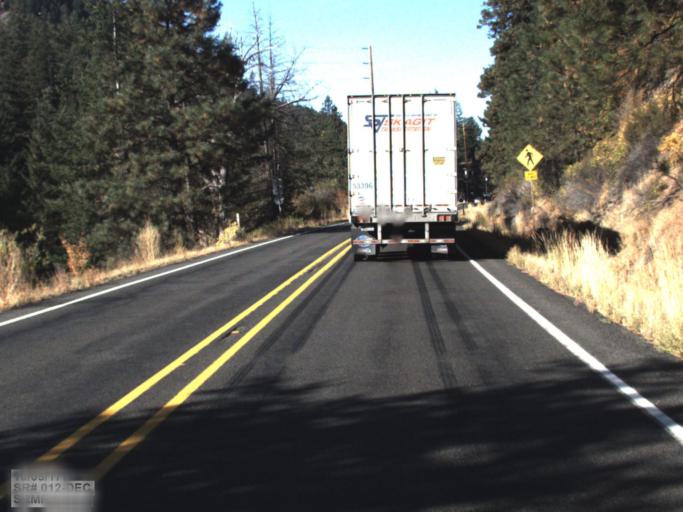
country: US
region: Washington
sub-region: Yakima County
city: Tieton
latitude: 46.6702
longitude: -120.9833
